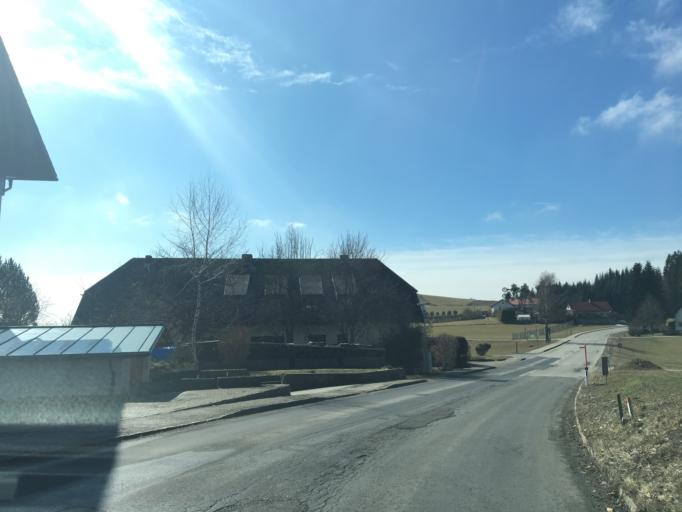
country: AT
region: Upper Austria
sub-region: Politischer Bezirk Perg
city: Sankt Georgen am Walde
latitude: 48.3639
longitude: 14.9096
